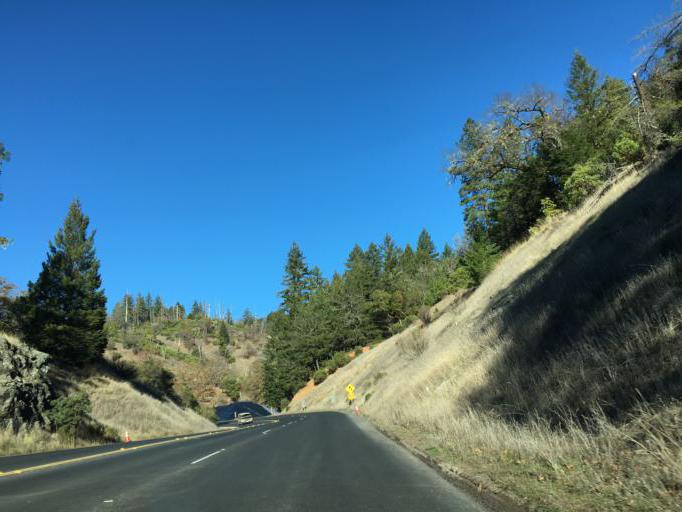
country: US
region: California
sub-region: Mendocino County
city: Laytonville
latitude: 39.7806
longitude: -123.5433
